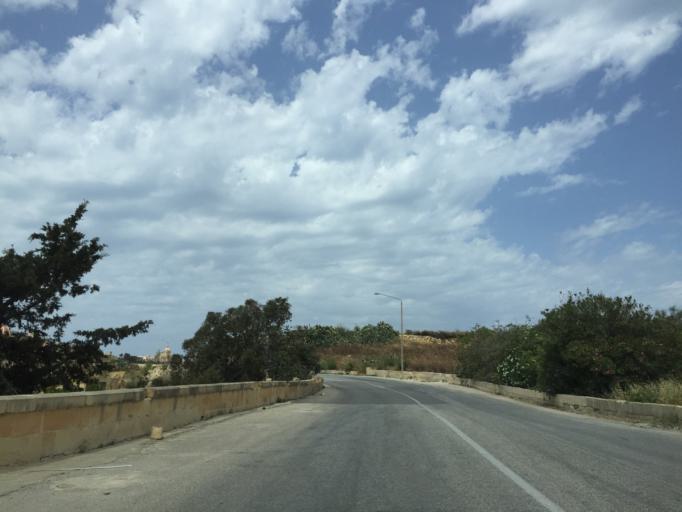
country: MT
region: Iz-Zebbug
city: Zebbug
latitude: 36.0595
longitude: 14.2371
